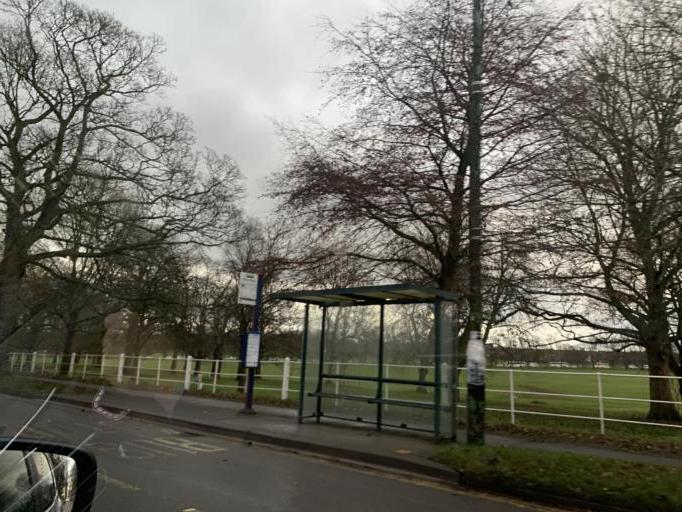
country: GB
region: England
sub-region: City of York
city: York
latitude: 53.9459
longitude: -1.1021
